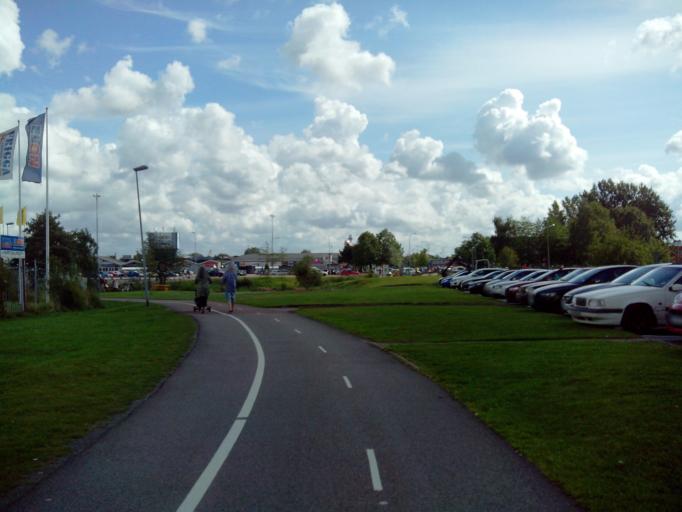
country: SE
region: Vaestra Goetaland
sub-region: Goteborg
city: Goeteborg
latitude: 57.7248
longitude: 11.9495
